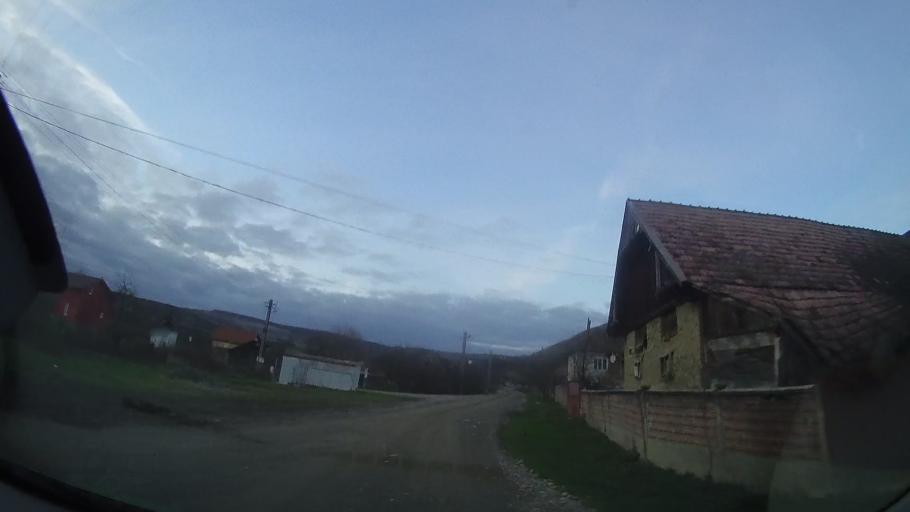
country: RO
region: Cluj
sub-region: Comuna Palatca
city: Palatca
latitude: 46.8658
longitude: 24.0171
